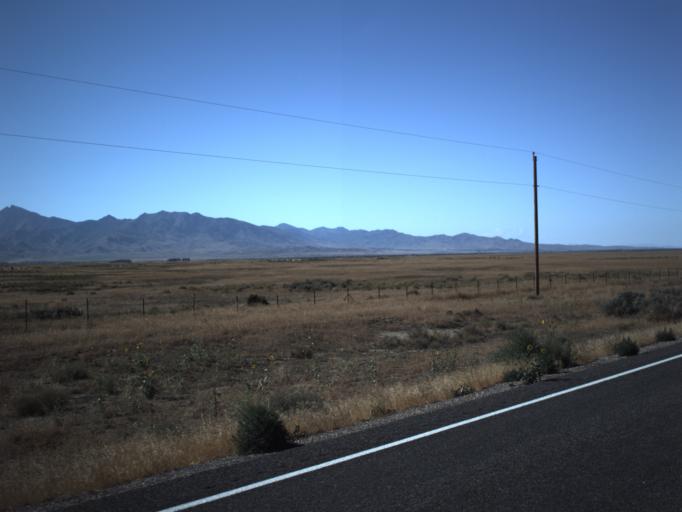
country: US
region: Utah
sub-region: Millard County
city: Delta
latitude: 39.5716
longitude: -112.3428
